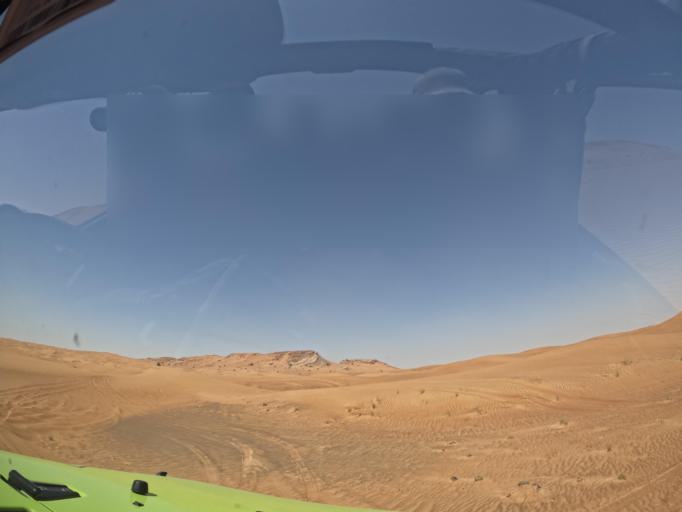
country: AE
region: Ash Shariqah
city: Adh Dhayd
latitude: 25.0200
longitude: 55.7402
